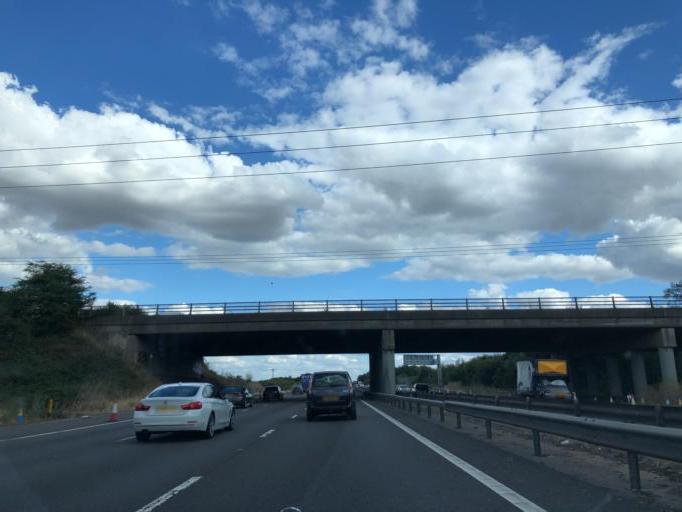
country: GB
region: England
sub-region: Milton Keynes
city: Newport Pagnell
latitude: 52.0731
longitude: -0.7303
